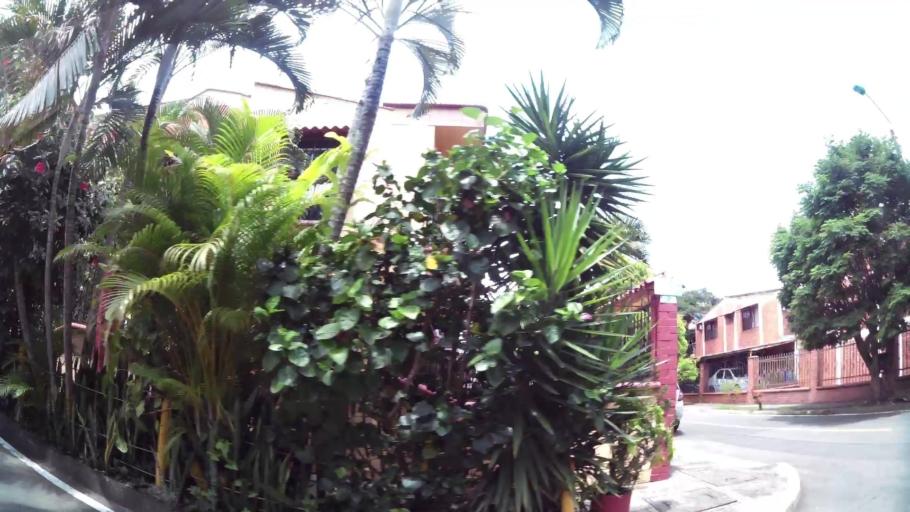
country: CO
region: Valle del Cauca
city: Cali
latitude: 3.3864
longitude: -76.5155
